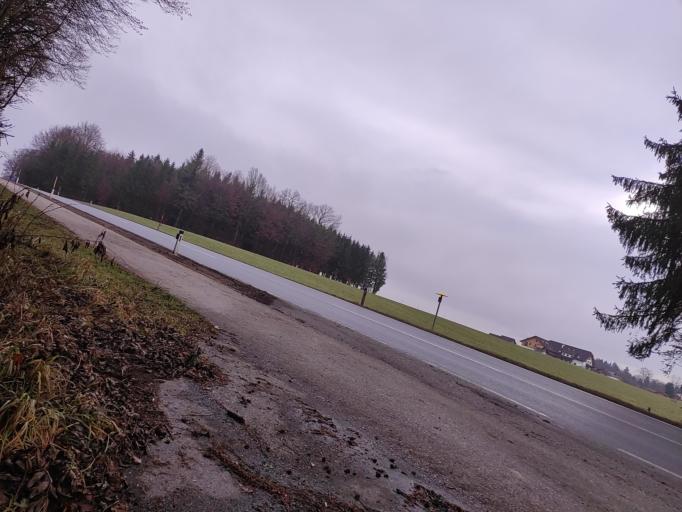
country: AT
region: Salzburg
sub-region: Politischer Bezirk Salzburg-Umgebung
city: Seekirchen am Wallersee
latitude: 47.9090
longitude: 13.1150
